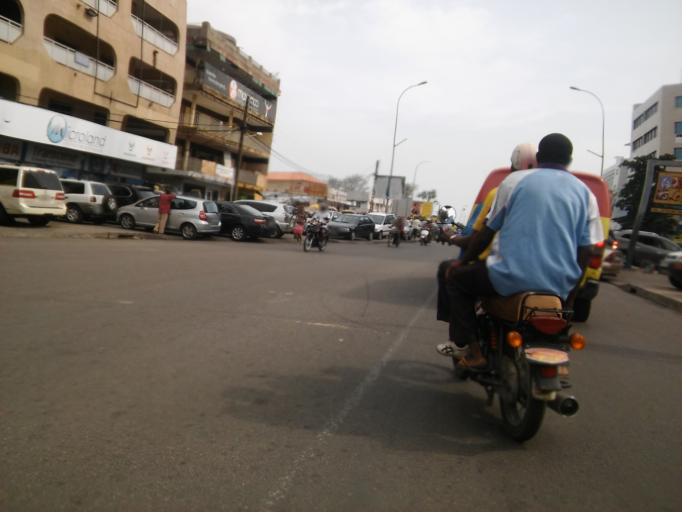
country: BJ
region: Littoral
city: Cotonou
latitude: 6.3566
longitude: 2.4390
